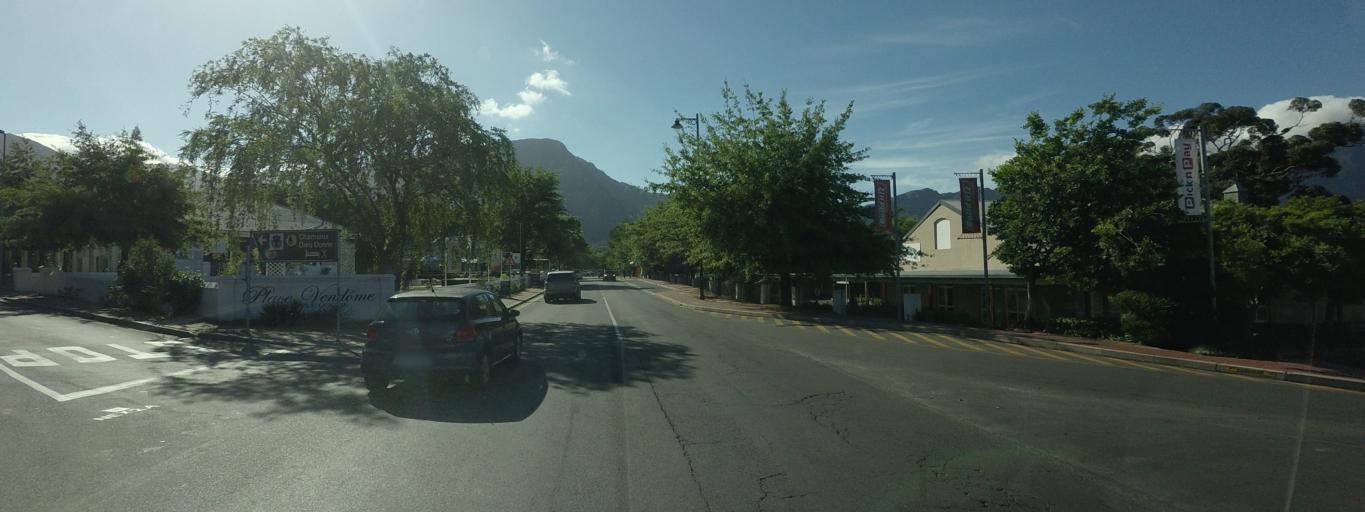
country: ZA
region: Western Cape
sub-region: Cape Winelands District Municipality
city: Paarl
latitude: -33.9057
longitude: 19.1141
